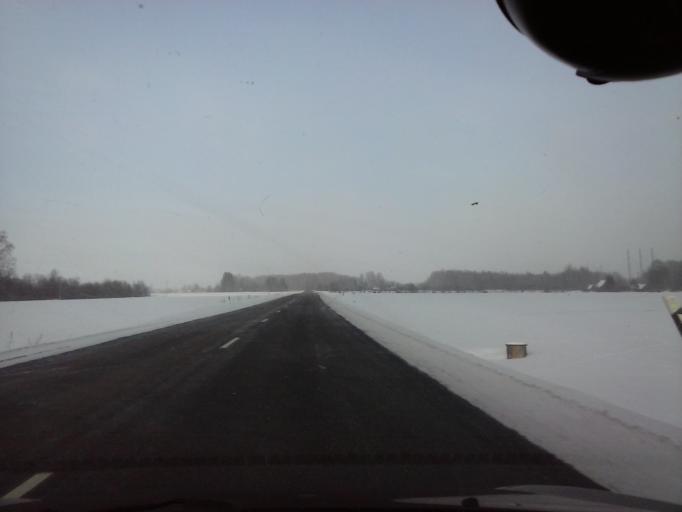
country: EE
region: Viljandimaa
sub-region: Abja vald
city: Abja-Paluoja
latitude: 58.2948
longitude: 25.2962
